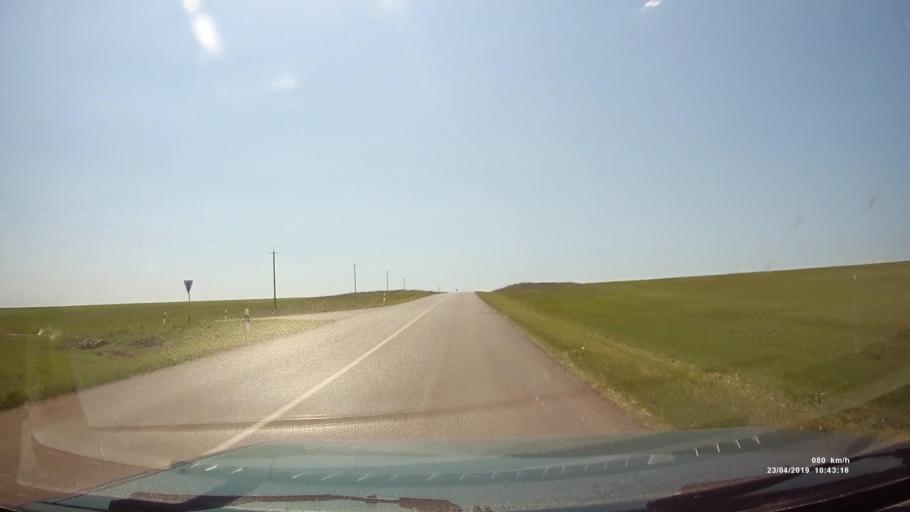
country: RU
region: Kalmykiya
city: Yashalta
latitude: 46.4722
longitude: 42.6491
